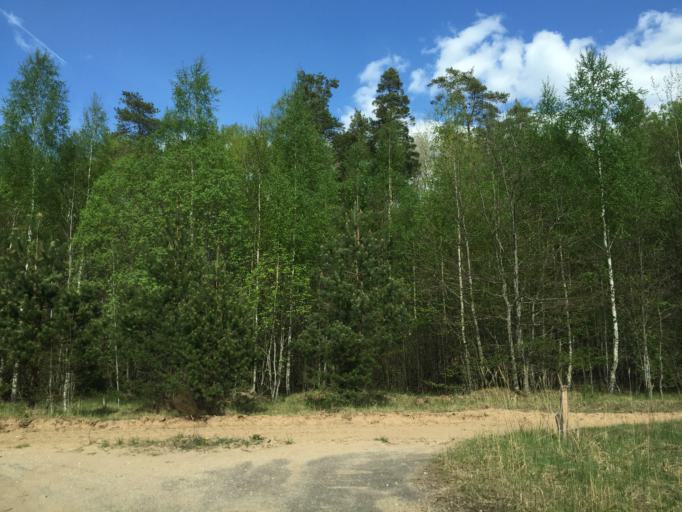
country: LV
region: Limbazu Rajons
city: Limbazi
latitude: 57.4176
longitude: 24.6887
